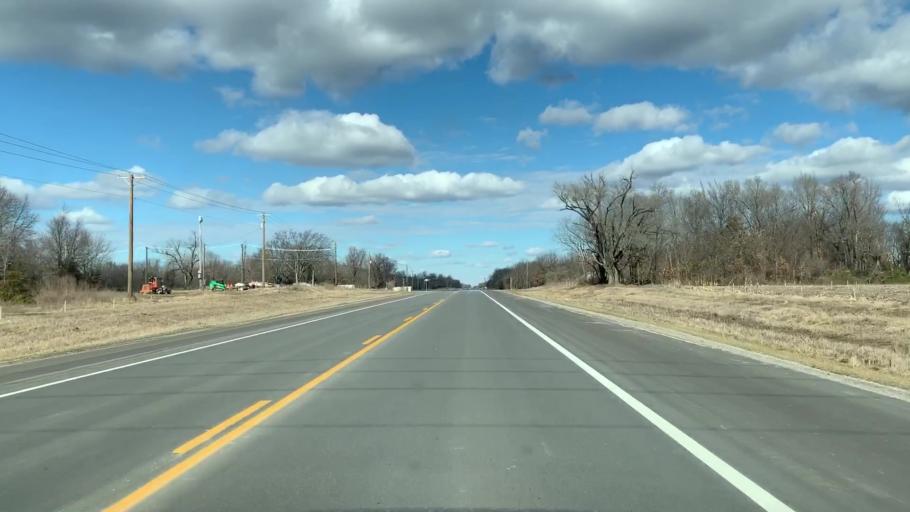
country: US
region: Kansas
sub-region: Cherokee County
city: Columbus
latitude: 37.2210
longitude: -94.8318
